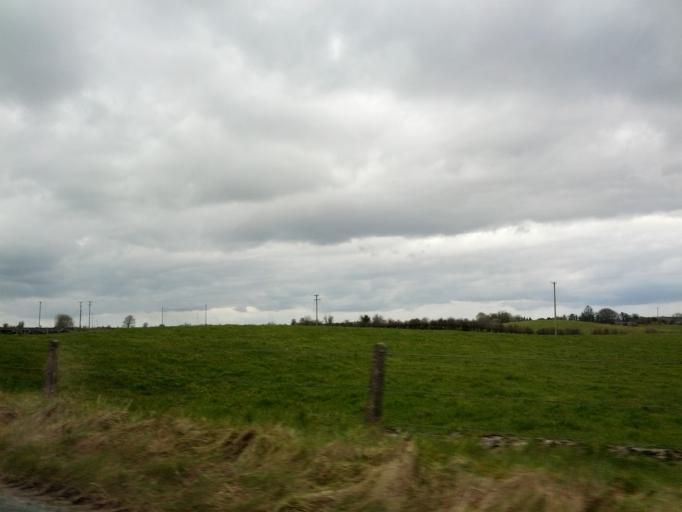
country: IE
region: Connaught
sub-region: County Galway
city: Athenry
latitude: 53.4116
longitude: -8.6347
